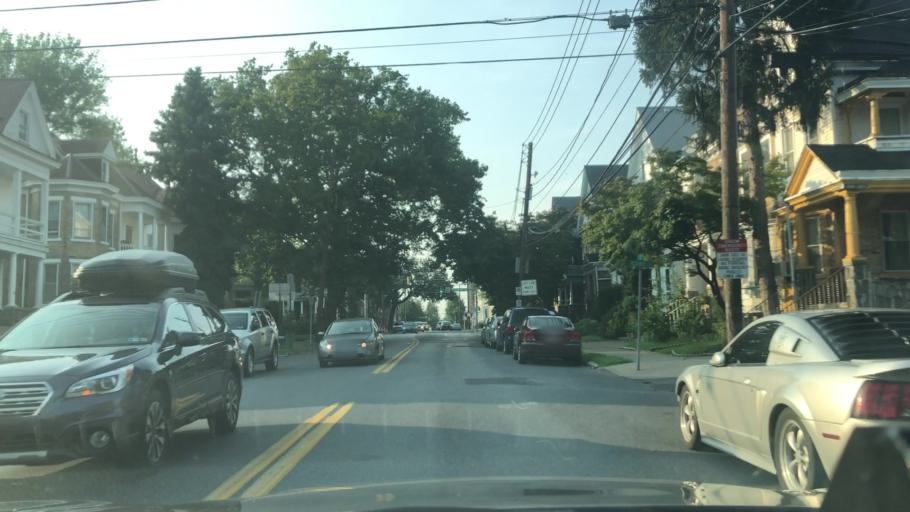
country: US
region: Pennsylvania
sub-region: Lehigh County
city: Allentown
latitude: 40.5983
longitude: -75.4883
